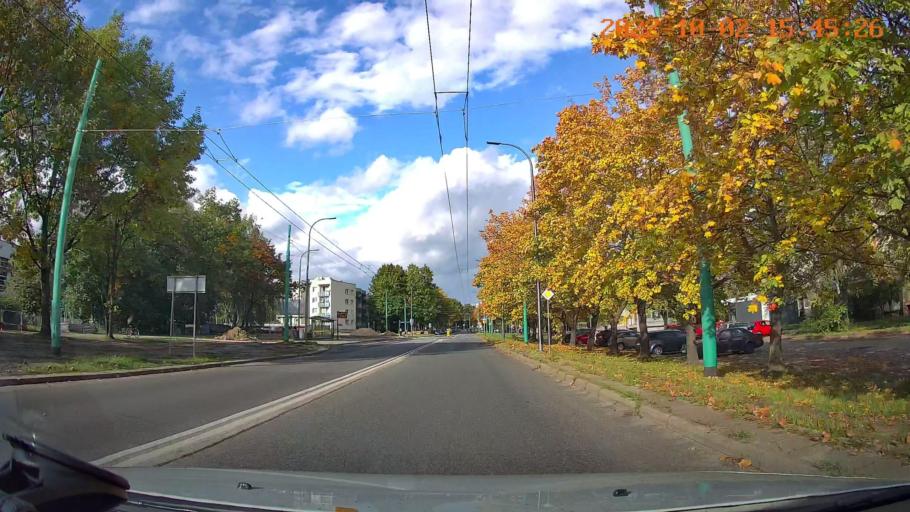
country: PL
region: Silesian Voivodeship
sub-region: Tychy
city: Cielmice
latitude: 50.0996
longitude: 18.9924
